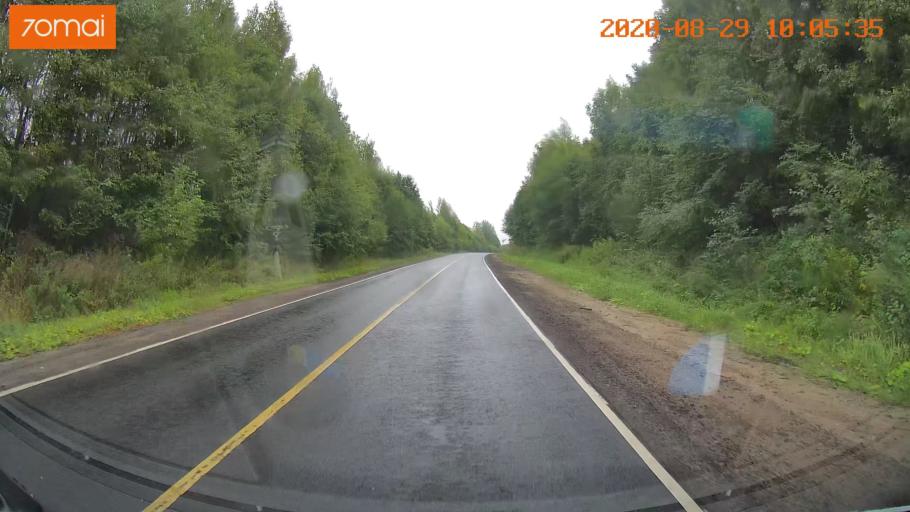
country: RU
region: Ivanovo
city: Zarechnyy
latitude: 57.3924
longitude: 42.5246
